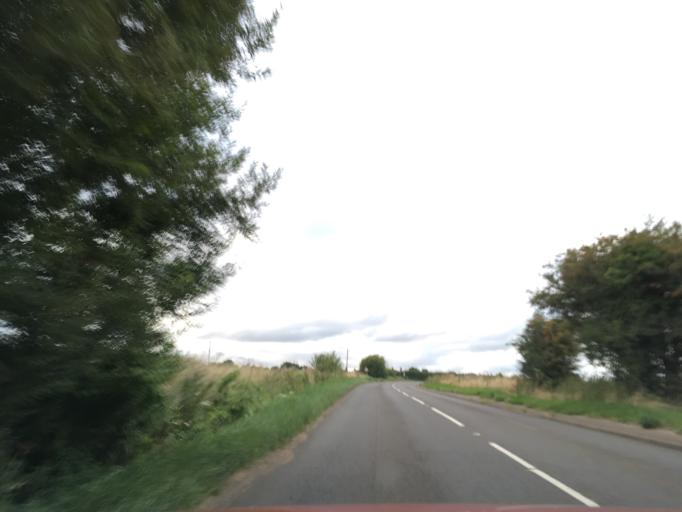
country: GB
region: England
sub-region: Wiltshire
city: Devizes
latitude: 51.3834
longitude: -2.0382
